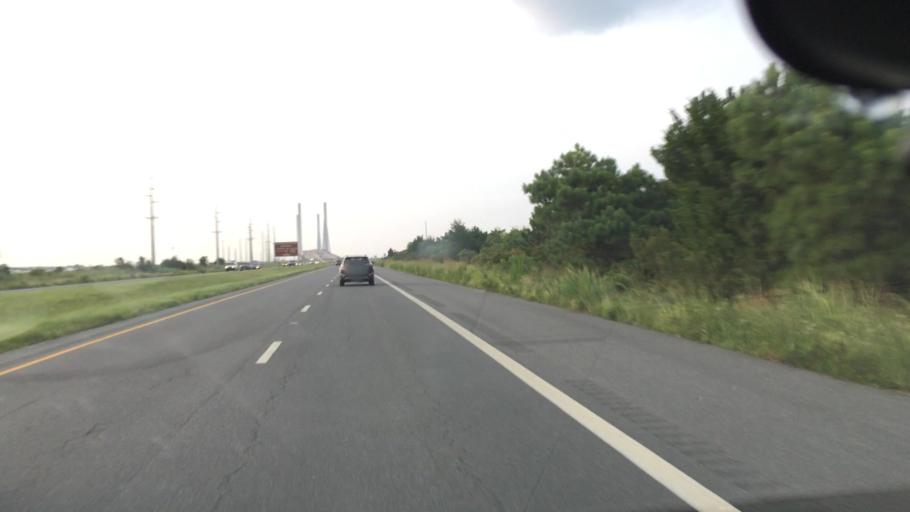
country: US
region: Delaware
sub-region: Sussex County
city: Bethany Beach
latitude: 38.5964
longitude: -75.0621
